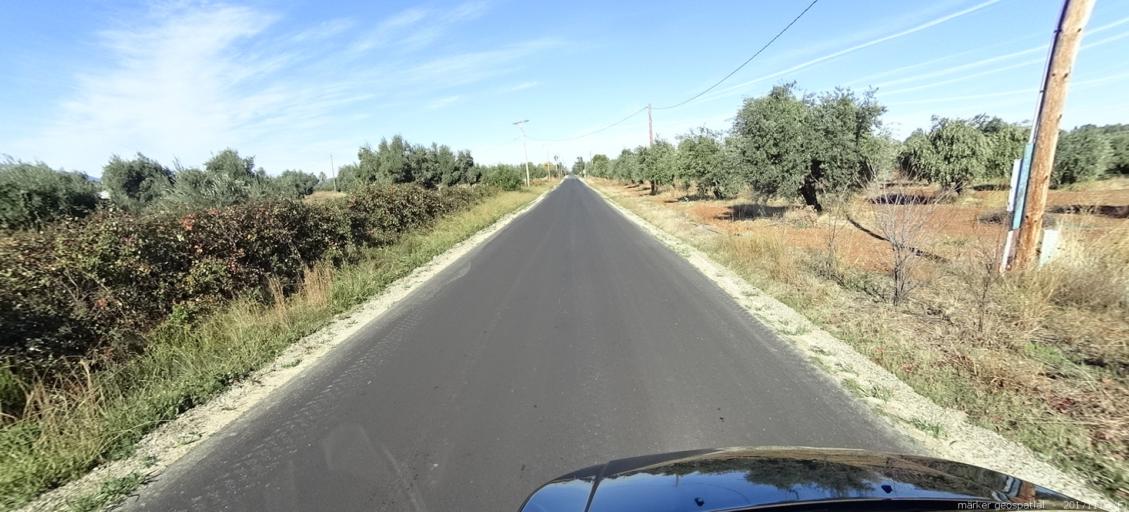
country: US
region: California
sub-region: Shasta County
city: Anderson
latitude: 40.4433
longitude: -122.4358
